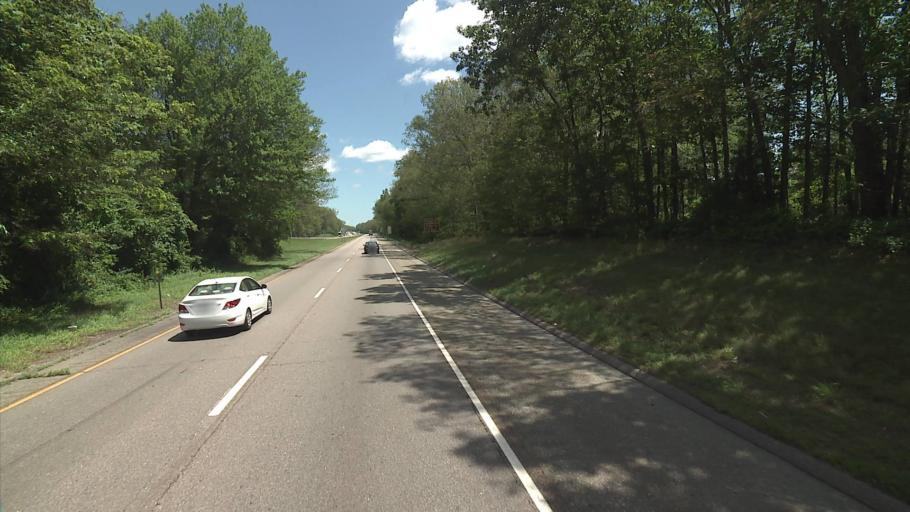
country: US
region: Connecticut
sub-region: New London County
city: Niantic
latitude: 41.3766
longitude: -72.1915
